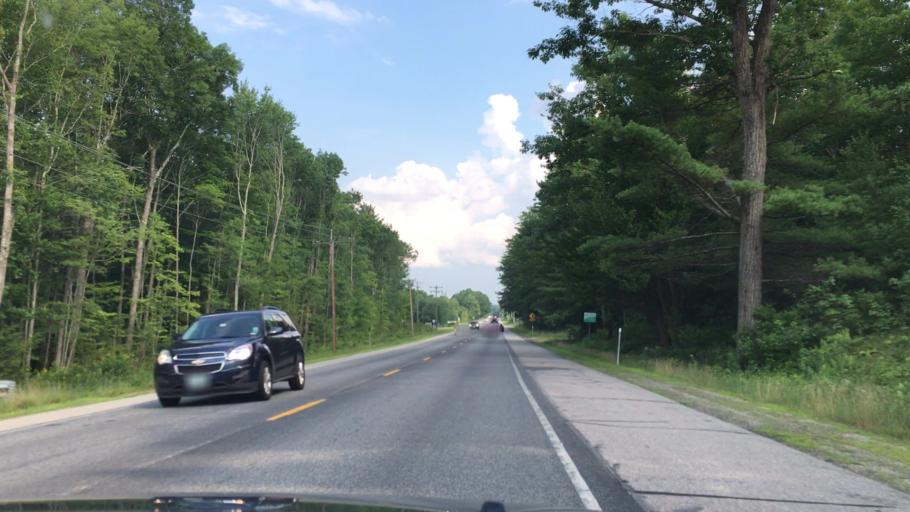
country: US
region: New Hampshire
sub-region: Strafford County
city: Farmington
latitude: 43.4011
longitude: -71.1098
